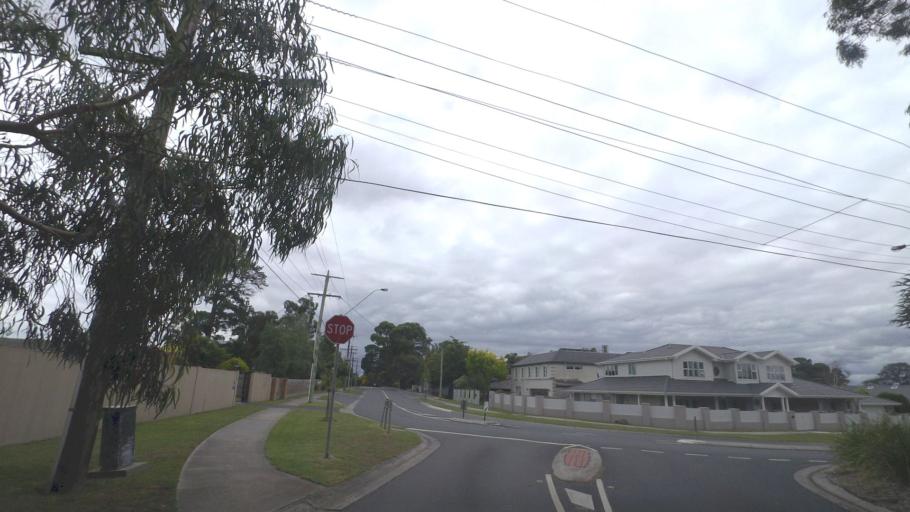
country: AU
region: Victoria
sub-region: Manningham
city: Park Orchards
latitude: -37.7839
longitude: 145.2274
